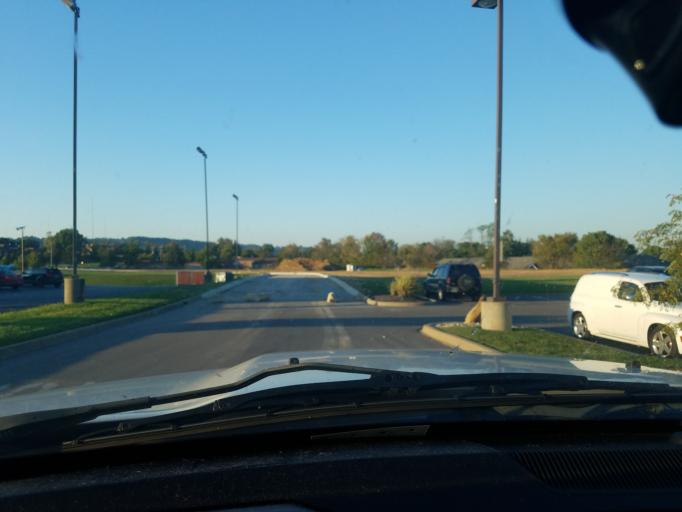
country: US
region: Indiana
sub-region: Floyd County
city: New Albany
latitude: 38.3397
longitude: -85.8156
